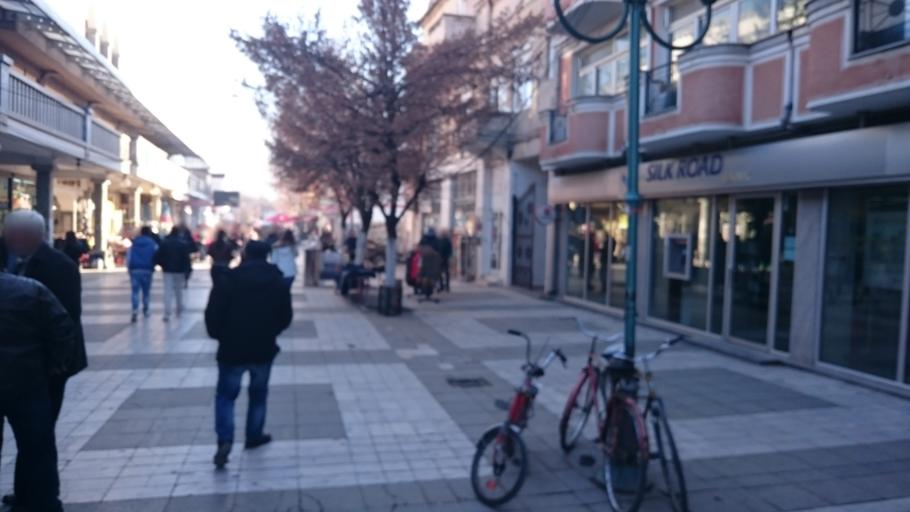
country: MK
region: Prilep
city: Prilep
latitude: 41.3448
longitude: 21.5545
